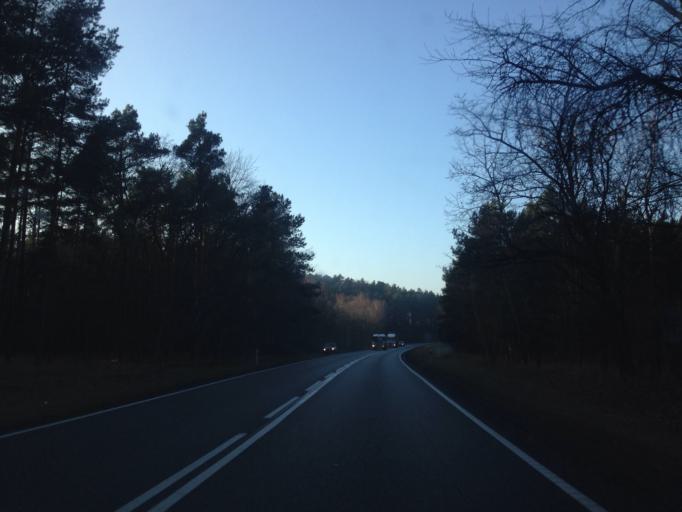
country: PL
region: Kujawsko-Pomorskie
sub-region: Powiat torunski
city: Zlawies Wielka
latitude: 53.0482
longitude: 18.3656
